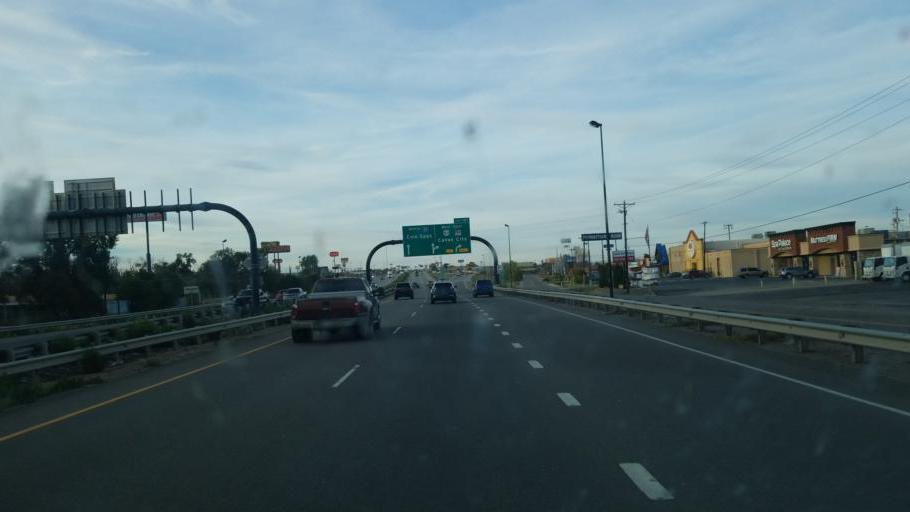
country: US
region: Colorado
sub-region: Pueblo County
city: Pueblo
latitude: 38.3008
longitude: -104.6122
